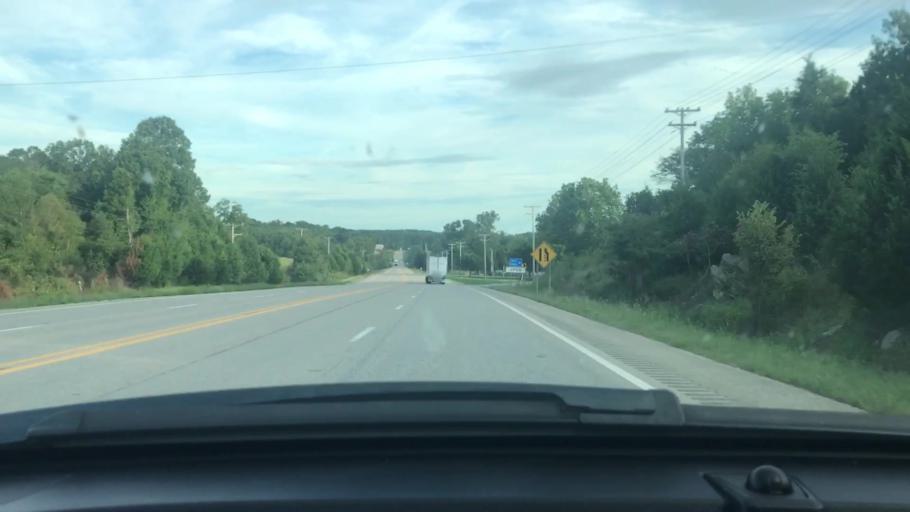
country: US
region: Arkansas
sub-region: Lawrence County
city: Hoxie
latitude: 36.1247
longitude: -91.1535
